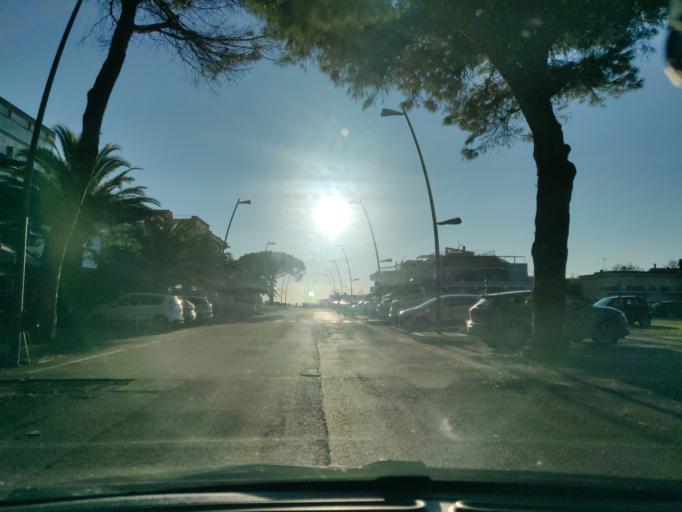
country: IT
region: Latium
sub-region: Provincia di Viterbo
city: Tarquinia
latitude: 42.2182
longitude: 11.7102
